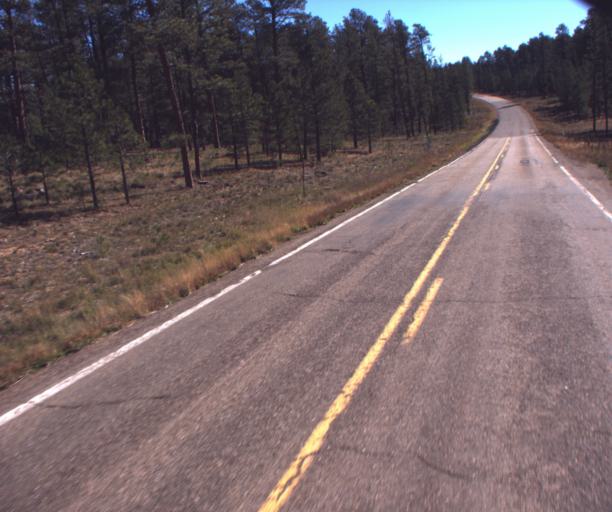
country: US
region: Arizona
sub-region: Coconino County
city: Fredonia
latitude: 36.7462
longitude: -112.2457
